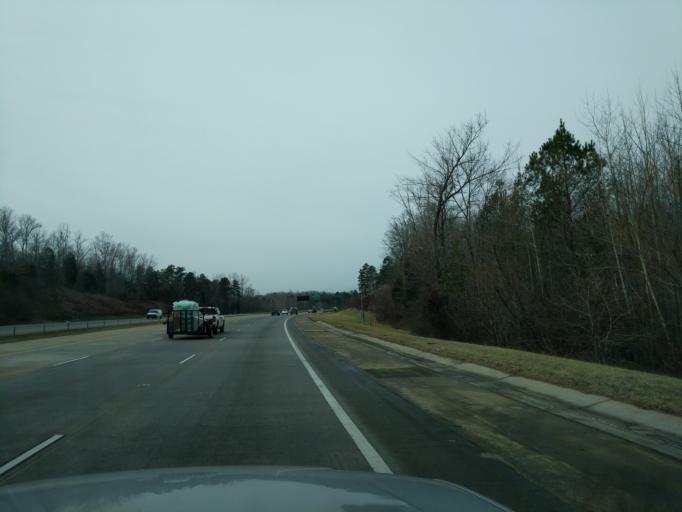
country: US
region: North Carolina
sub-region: Mecklenburg County
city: Huntersville
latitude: 35.3402
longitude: -80.8885
